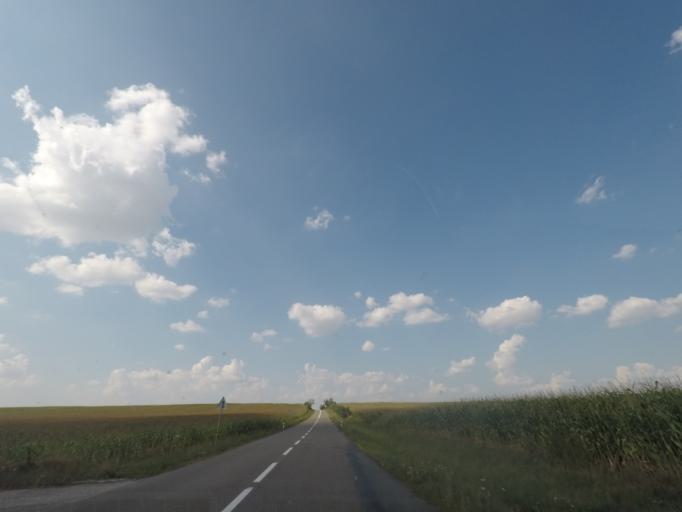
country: CZ
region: Kralovehradecky
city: Dolni Cernilov
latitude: 50.2332
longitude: 15.9689
